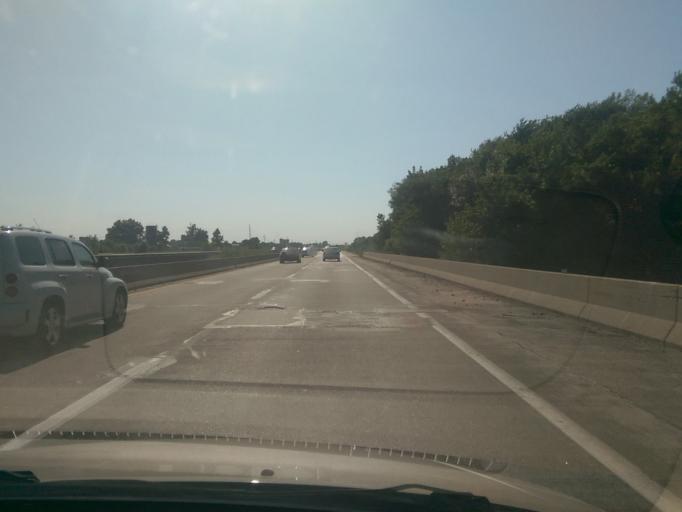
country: US
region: Missouri
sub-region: Saline County
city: Sweet Springs
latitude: 38.9779
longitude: -93.4370
